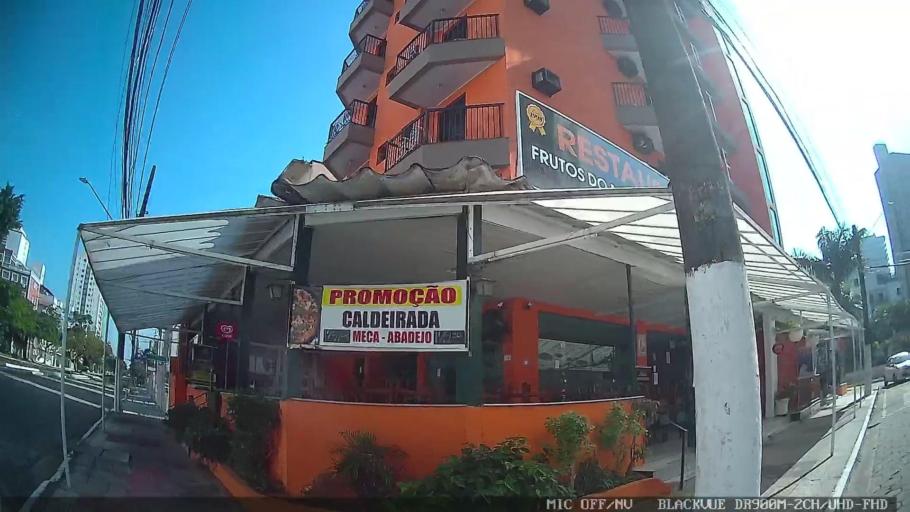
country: BR
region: Sao Paulo
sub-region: Guaruja
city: Guaruja
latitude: -24.0094
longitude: -46.2718
